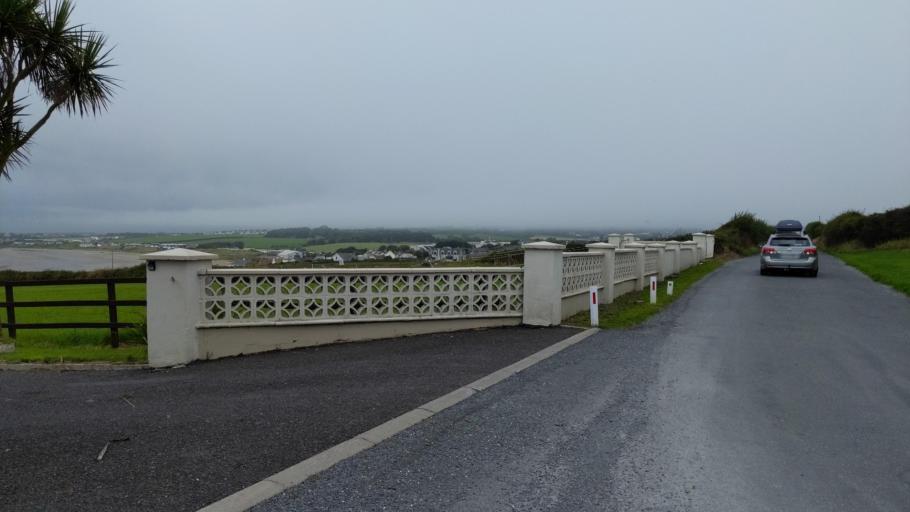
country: IE
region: Leinster
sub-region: Lu
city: Clogherhead
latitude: 53.7918
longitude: -6.2284
